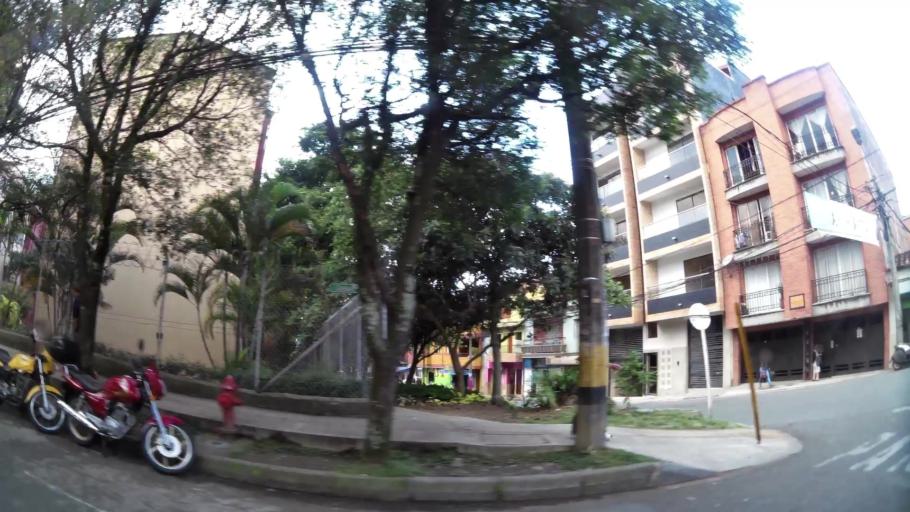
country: CO
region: Antioquia
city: Envigado
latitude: 6.1611
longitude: -75.5819
